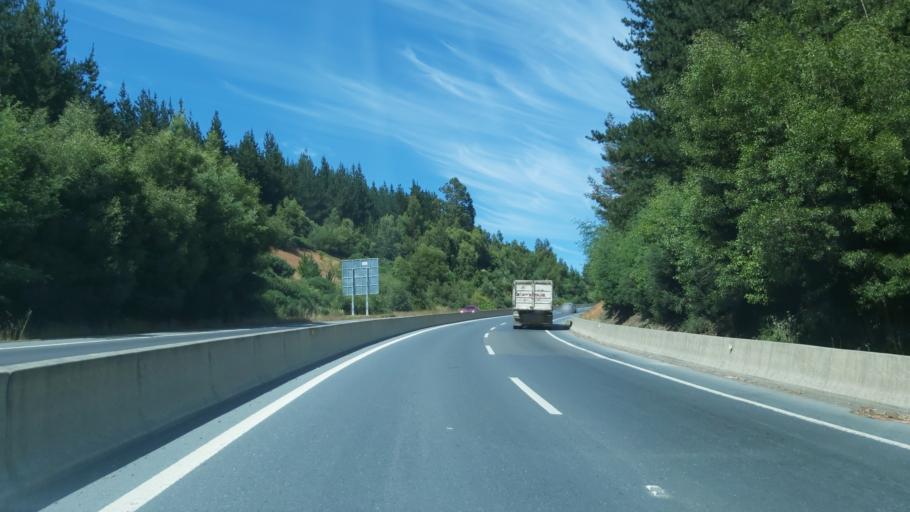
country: CL
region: Biobio
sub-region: Provincia de Concepcion
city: Lota
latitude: -37.0817
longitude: -73.1370
